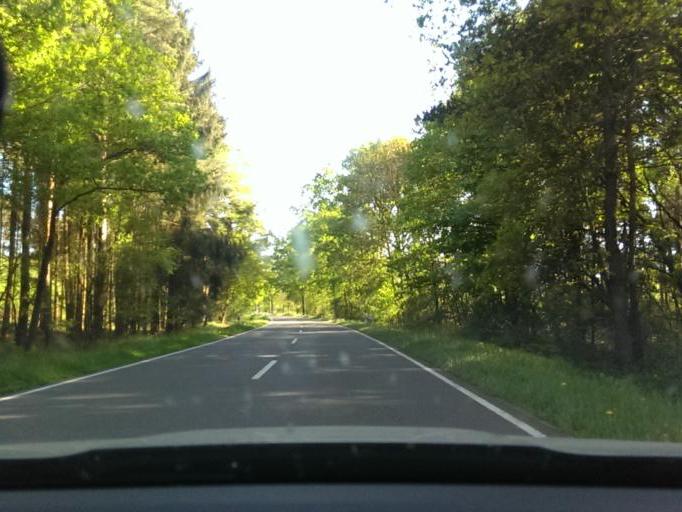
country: DE
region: Lower Saxony
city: Hambuhren
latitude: 52.6014
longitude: 9.9279
